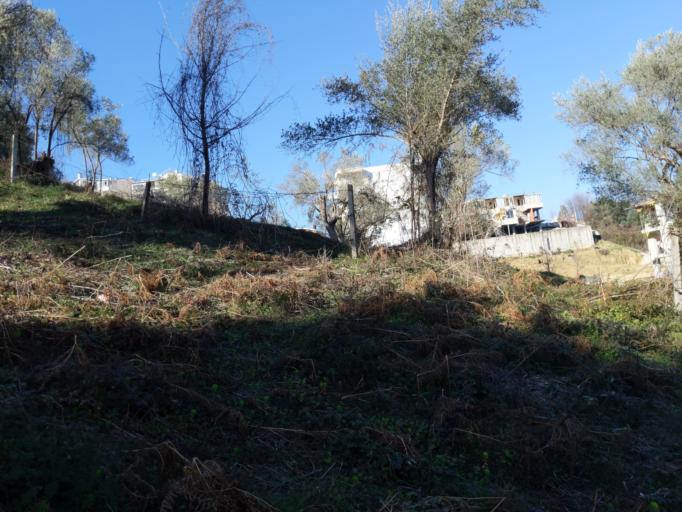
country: AL
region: Tirane
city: Tirana
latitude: 41.3089
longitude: 19.8024
